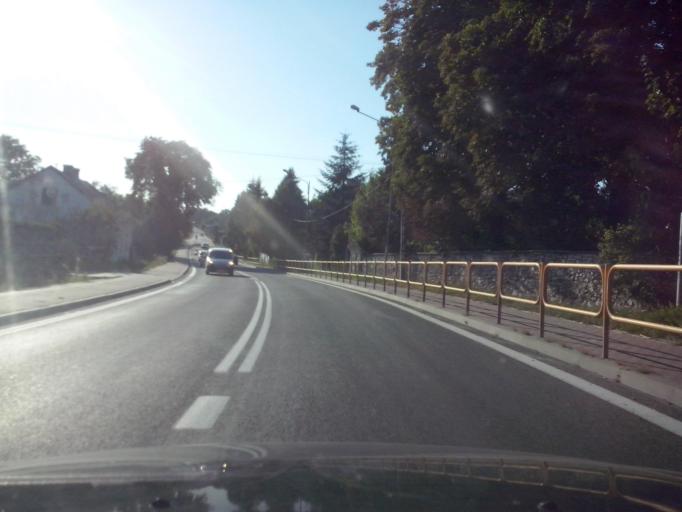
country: PL
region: Swietokrzyskie
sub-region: Powiat kielecki
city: Pierzchnica
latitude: 50.6685
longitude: 20.6738
